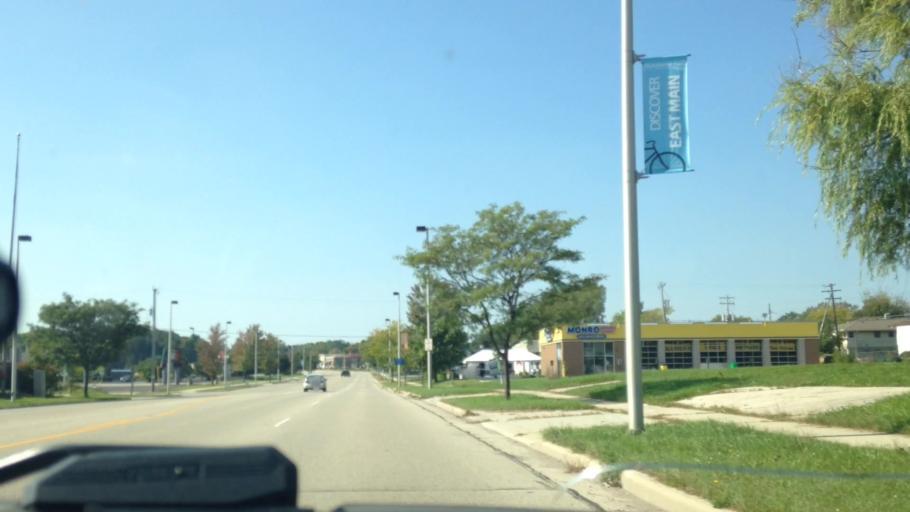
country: US
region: Wisconsin
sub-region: Waukesha County
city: Menomonee Falls
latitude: 43.1777
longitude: -88.0973
